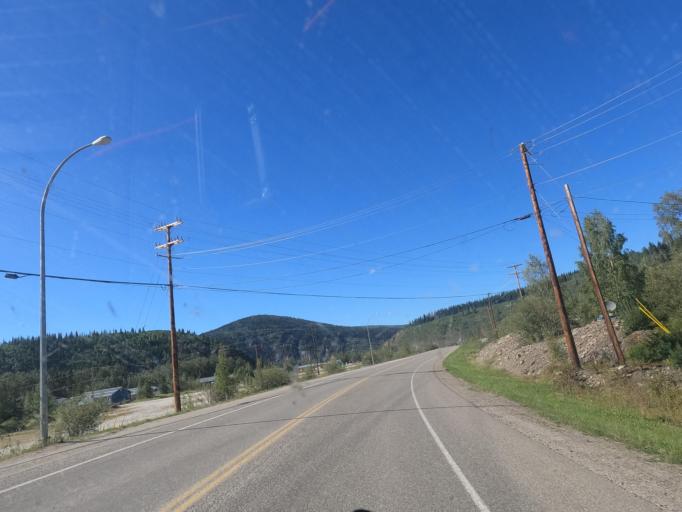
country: CA
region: Yukon
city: Dawson City
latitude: 64.0445
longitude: -139.4174
